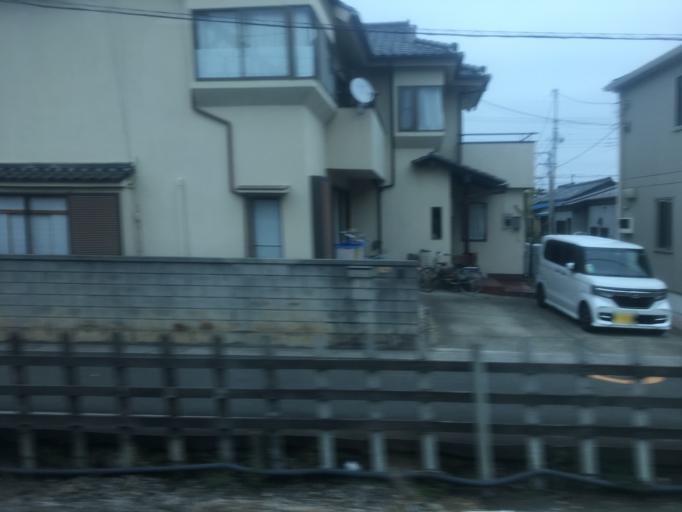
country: JP
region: Saitama
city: Ageoshimo
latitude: 35.9786
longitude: 139.5840
